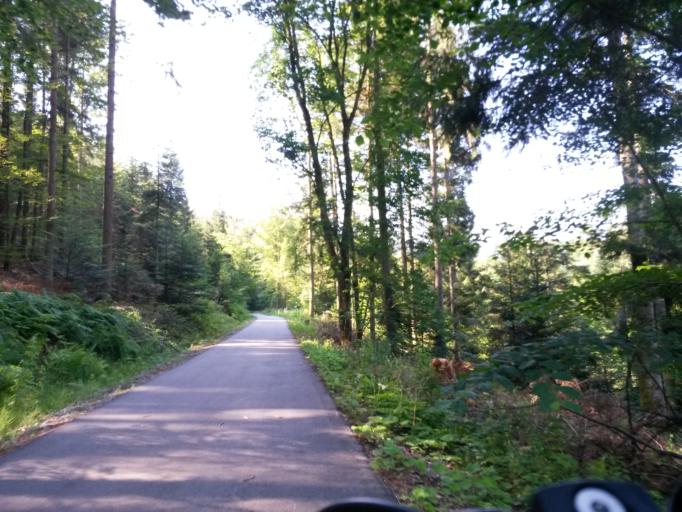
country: DE
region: Baden-Wuerttemberg
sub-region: Karlsruhe Region
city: Bad Wildbad
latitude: 48.7125
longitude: 8.5443
